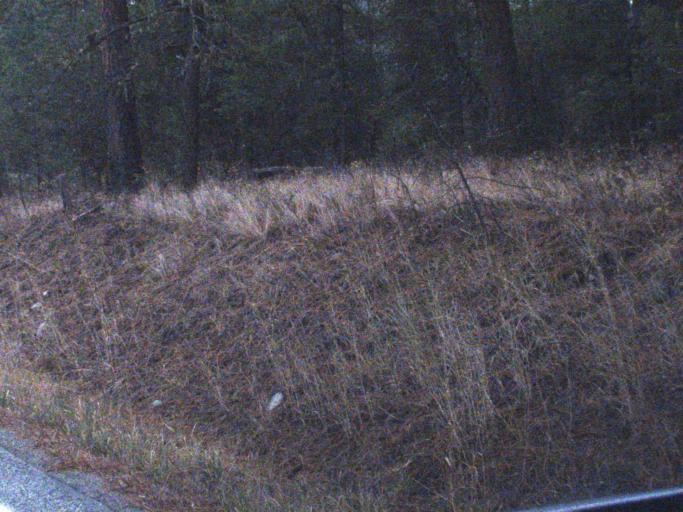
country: CA
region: British Columbia
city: Grand Forks
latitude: 48.9097
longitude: -118.2050
